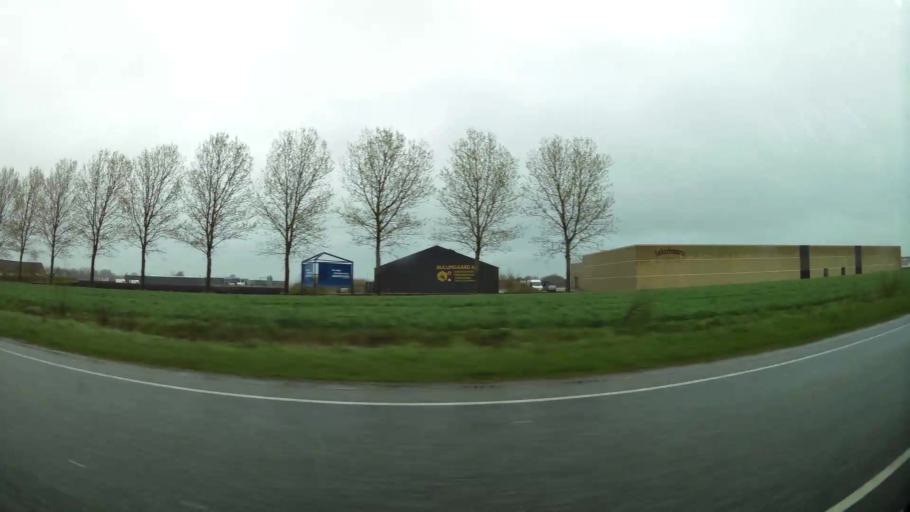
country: DK
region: Central Jutland
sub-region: Herning Kommune
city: Avlum
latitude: 56.2531
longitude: 8.7909
